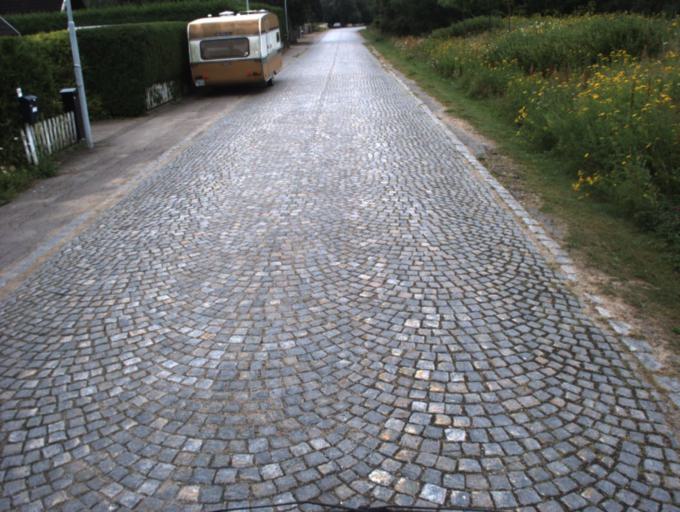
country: SE
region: Skane
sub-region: Helsingborg
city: Odakra
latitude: 56.0862
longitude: 12.7500
